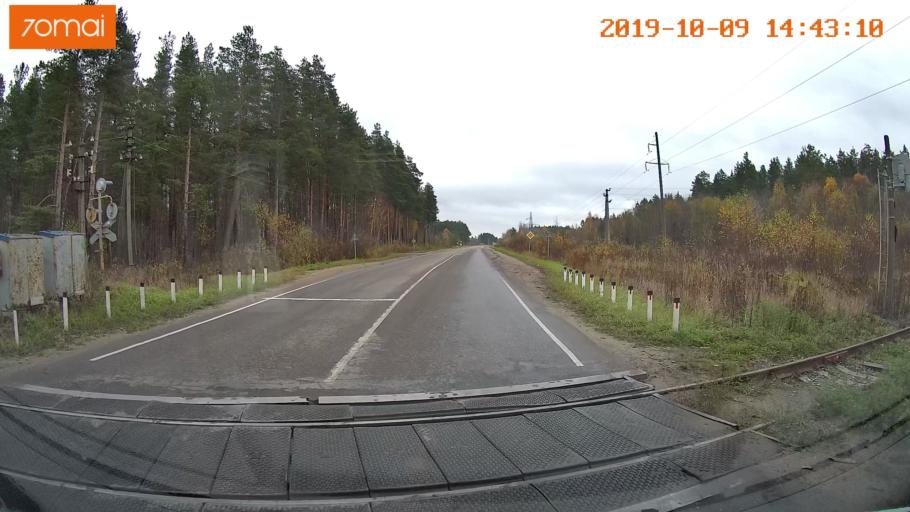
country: RU
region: Kostroma
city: Buy
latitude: 58.4583
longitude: 41.5423
